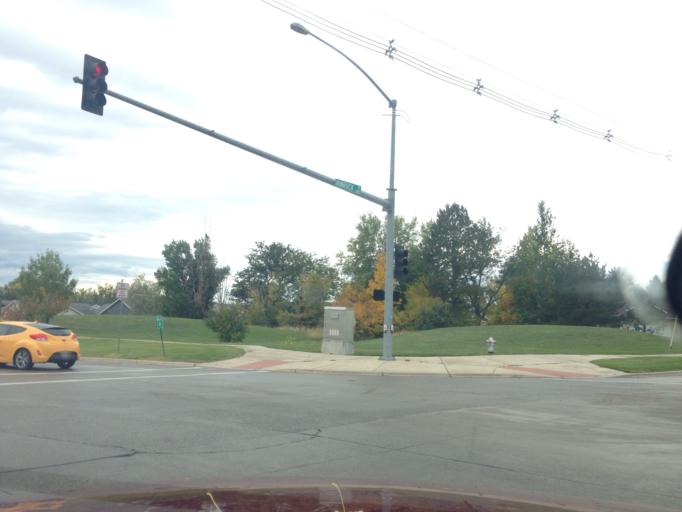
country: US
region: Montana
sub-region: Yellowstone County
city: Billings
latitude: 45.7985
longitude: -108.6181
